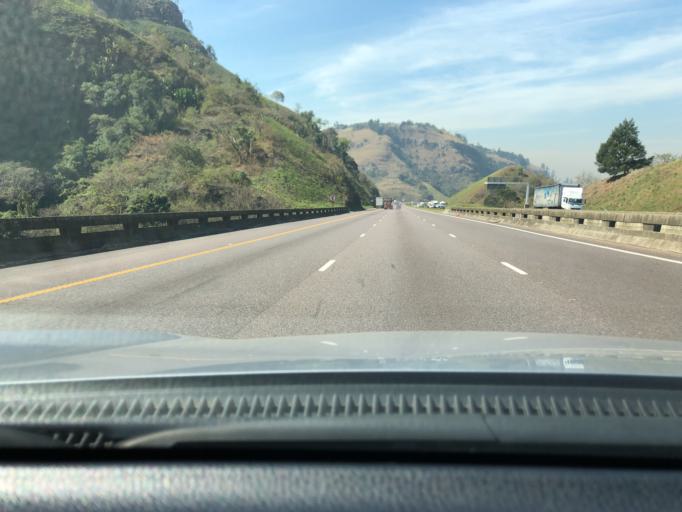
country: ZA
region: KwaZulu-Natal
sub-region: eThekwini Metropolitan Municipality
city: Mpumalanga
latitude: -29.8104
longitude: 30.7618
